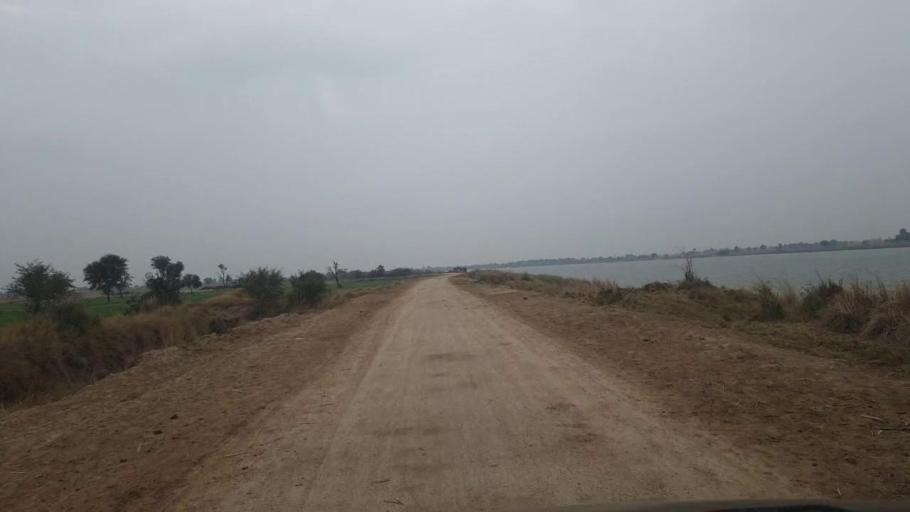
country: PK
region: Sindh
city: Tando Adam
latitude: 25.8470
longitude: 68.6985
